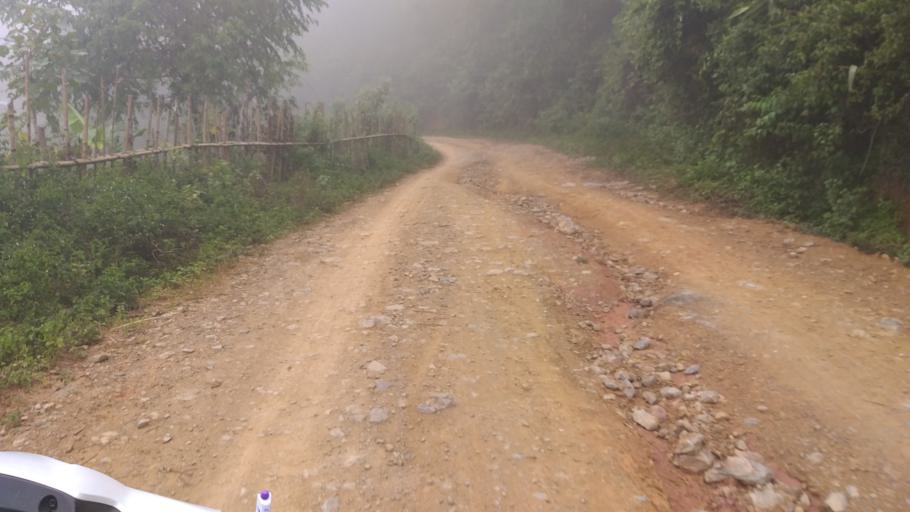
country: LA
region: Phongsali
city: Khoa
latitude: 21.2582
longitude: 102.6661
